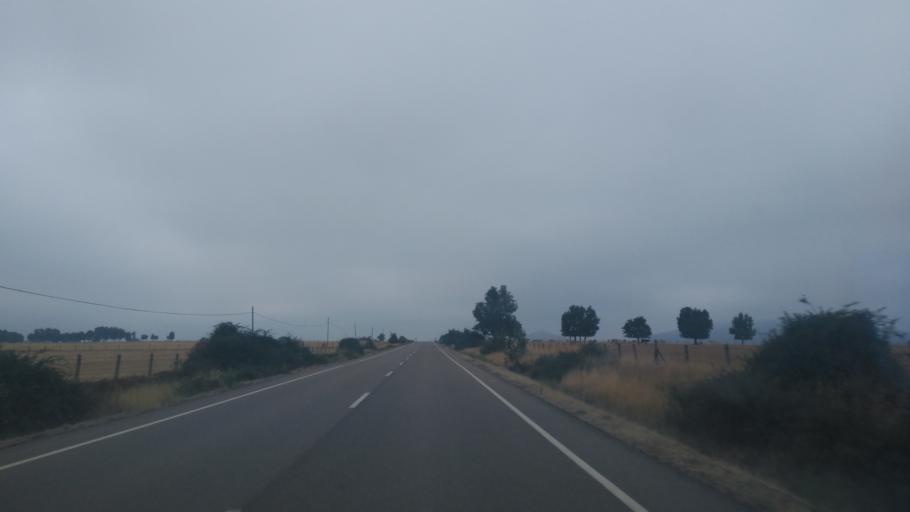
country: ES
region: Castille and Leon
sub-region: Provincia de Salamanca
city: Tamames
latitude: 40.6402
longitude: -6.1121
